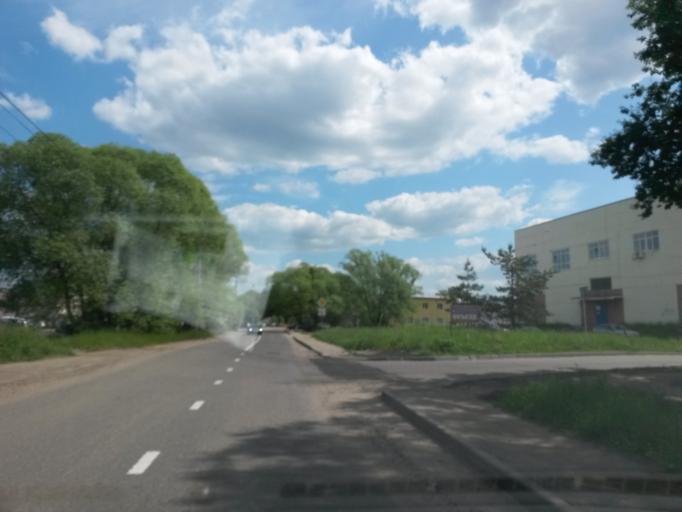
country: RU
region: Jaroslavl
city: Yaroslavl
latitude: 57.5921
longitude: 39.8831
